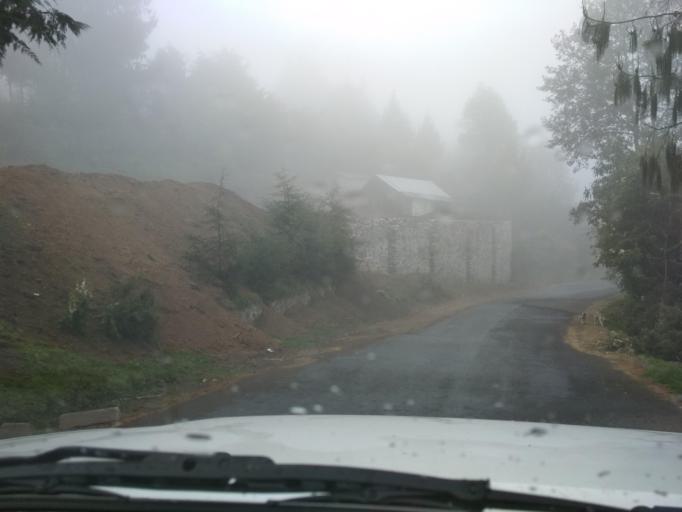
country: MX
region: Veracruz
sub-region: Mariano Escobedo
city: San Isidro el Berro
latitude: 18.9306
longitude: -97.2154
